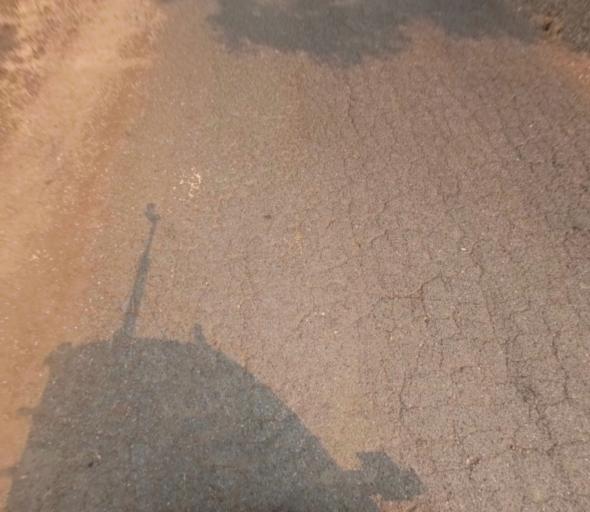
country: US
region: California
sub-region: Madera County
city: Oakhurst
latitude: 37.3006
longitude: -119.6035
